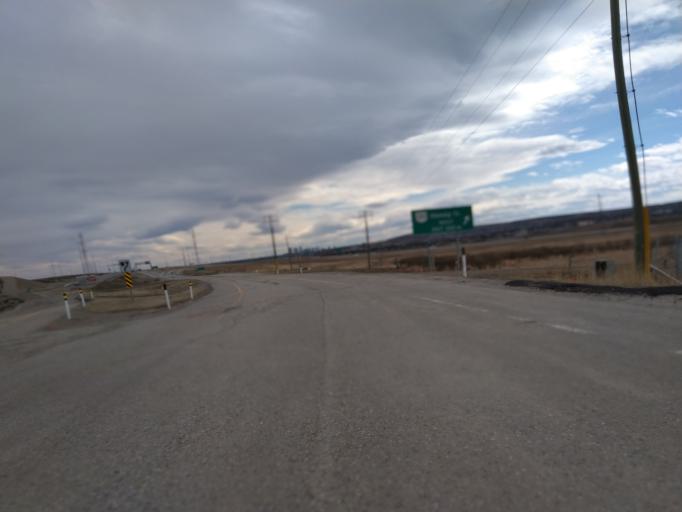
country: CA
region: Alberta
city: Airdrie
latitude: 51.1791
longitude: -114.0713
